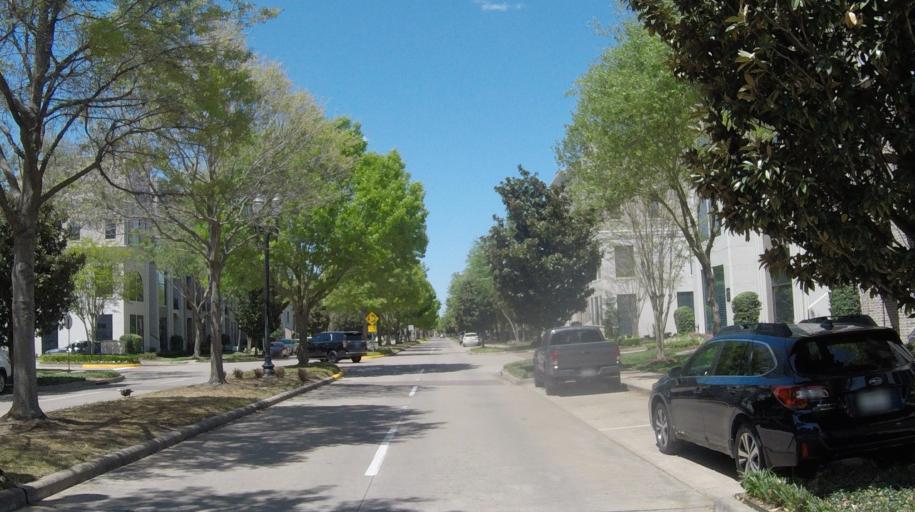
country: US
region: Texas
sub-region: Fort Bend County
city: Sugar Land
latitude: 29.6034
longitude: -95.6212
